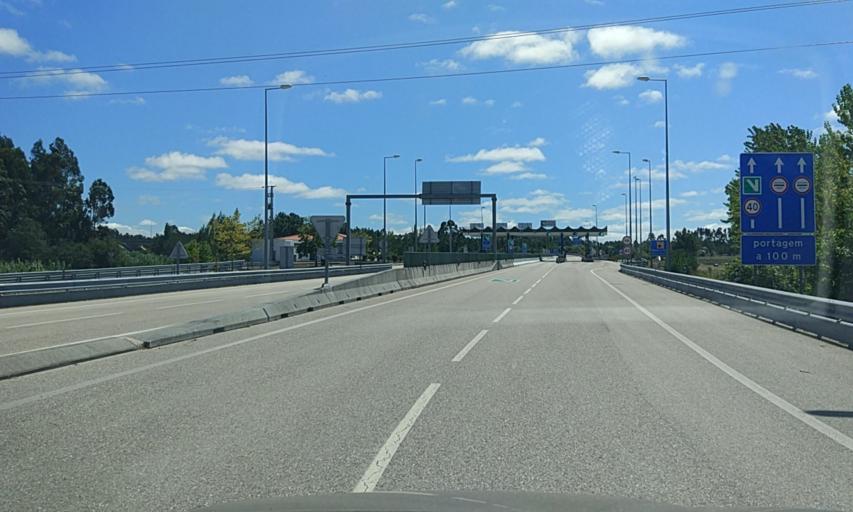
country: PT
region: Coimbra
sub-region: Montemor-O-Velho
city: Arazede
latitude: 40.3306
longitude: -8.7269
